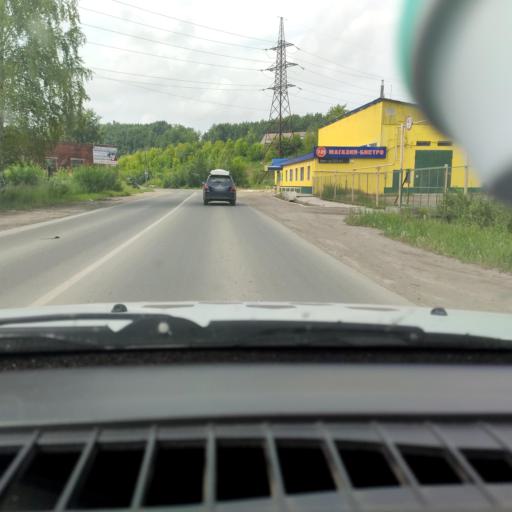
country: RU
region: Perm
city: Chusovoy
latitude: 58.3012
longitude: 57.8111
